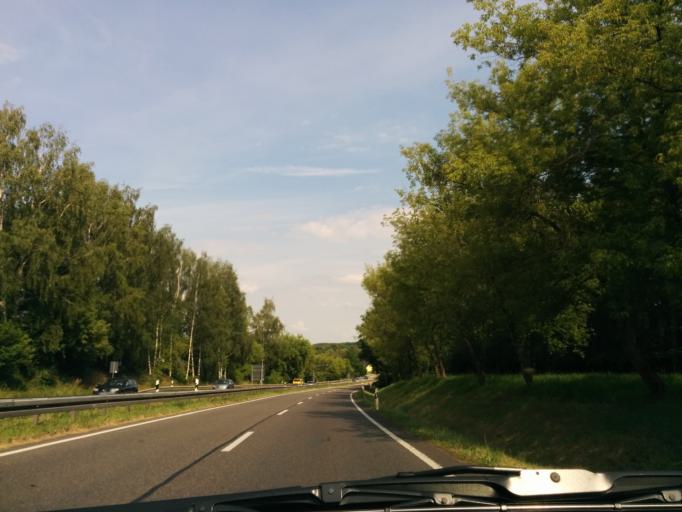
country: DE
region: Saxony
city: Niederwiesa
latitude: 50.8623
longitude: 13.0084
